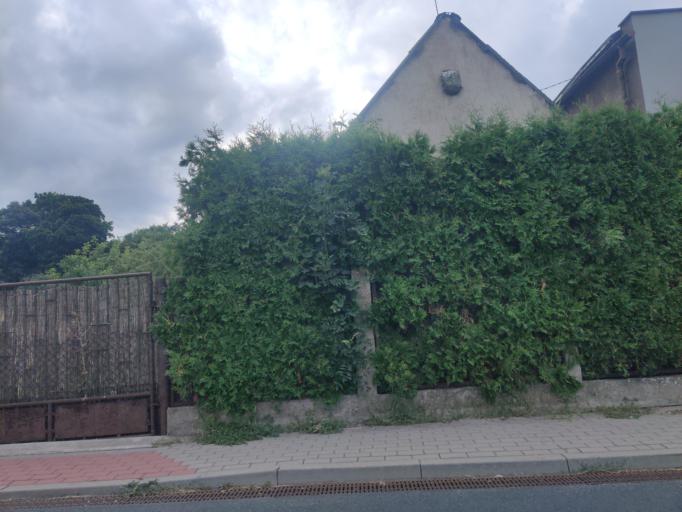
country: PL
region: Greater Poland Voivodeship
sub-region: Konin
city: Konin
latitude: 52.1961
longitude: 18.3054
